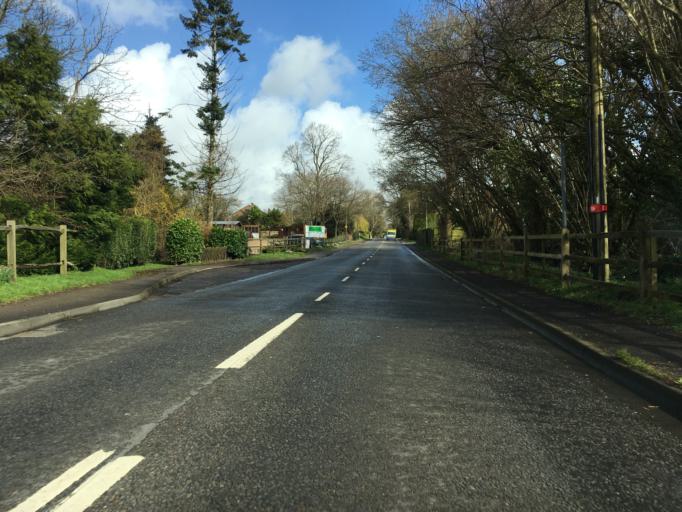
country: GB
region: England
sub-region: Hampshire
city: Compton
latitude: 51.0135
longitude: -1.3401
